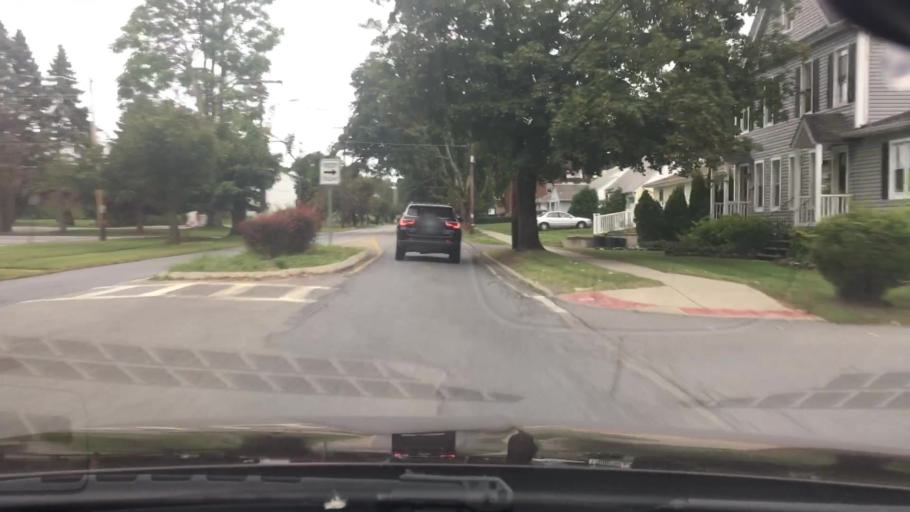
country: US
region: New York
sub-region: Dutchess County
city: Arlington
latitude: 41.6882
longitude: -73.9089
